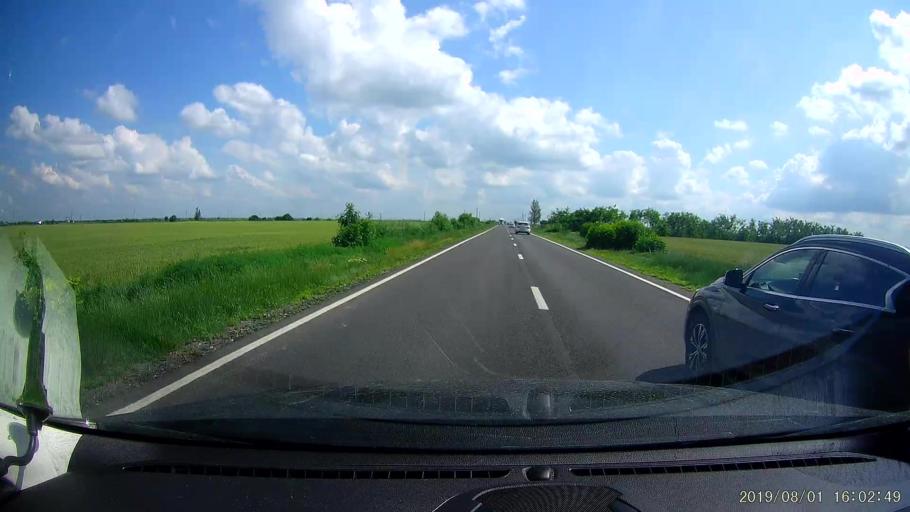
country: RO
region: Calarasi
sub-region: Comuna Dragalina
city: Drajna Noua
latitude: 44.4832
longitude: 27.3863
